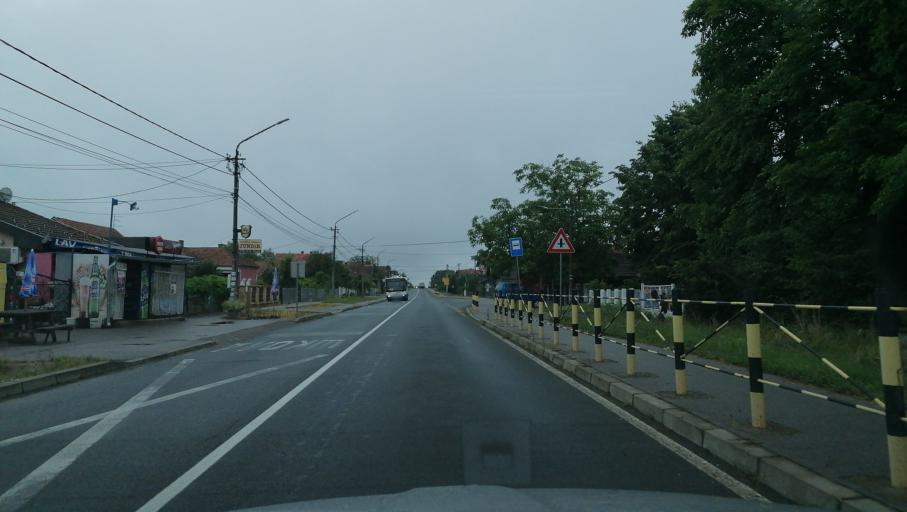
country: RS
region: Central Serbia
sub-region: Rasinski Okrug
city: Krusevac
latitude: 43.5877
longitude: 21.2716
